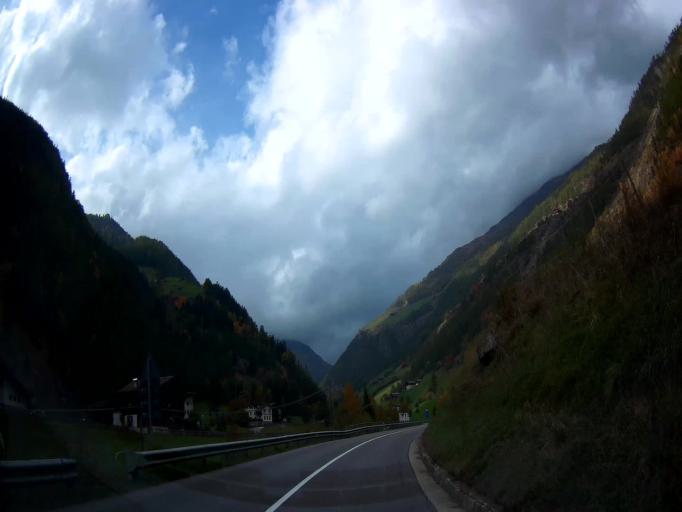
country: IT
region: Trentino-Alto Adige
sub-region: Bolzano
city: Senales
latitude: 46.7088
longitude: 10.9047
